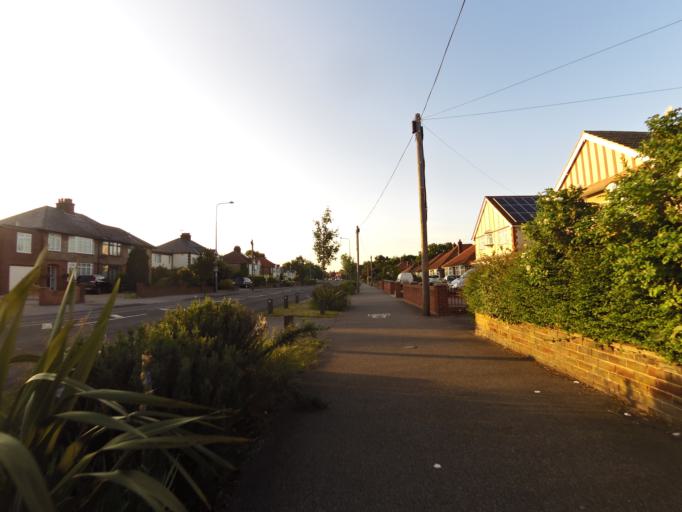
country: GB
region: England
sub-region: Suffolk
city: Kesgrave
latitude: 52.0534
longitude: 1.2019
